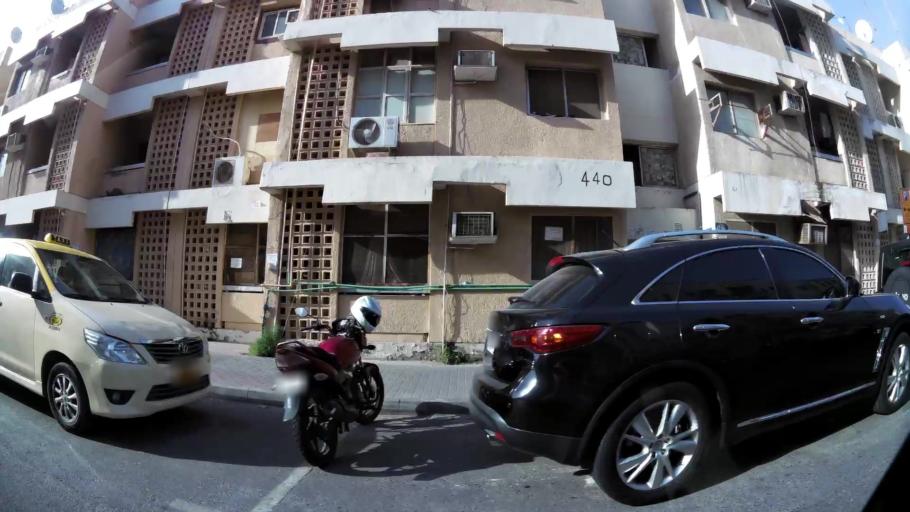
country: AE
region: Ash Shariqah
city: Sharjah
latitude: 25.2415
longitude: 55.3025
